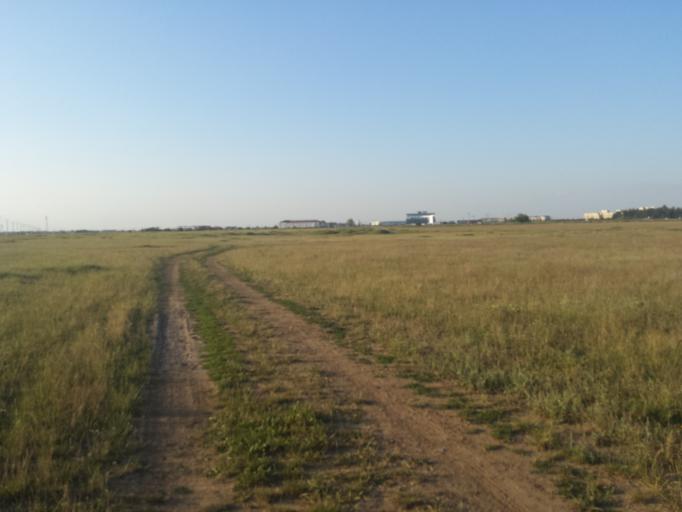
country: RO
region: Ilfov
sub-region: Comuna Tunari
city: Tunari
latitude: 44.5209
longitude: 26.1526
